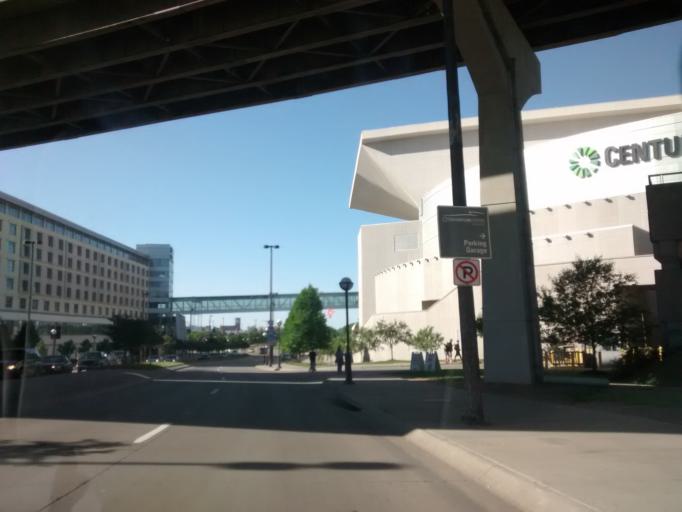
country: US
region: Nebraska
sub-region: Douglas County
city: Omaha
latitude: 41.2616
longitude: -95.9291
